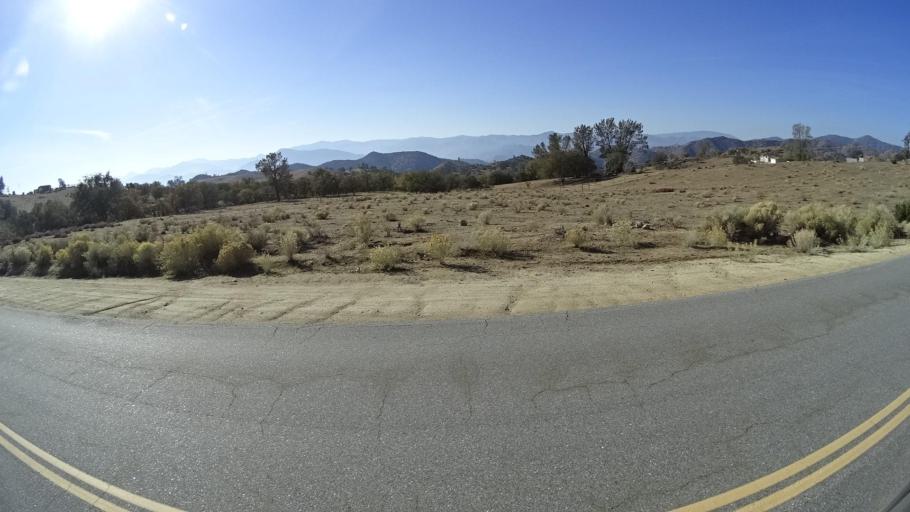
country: US
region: California
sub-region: Kern County
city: Bodfish
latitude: 35.3694
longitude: -118.3921
